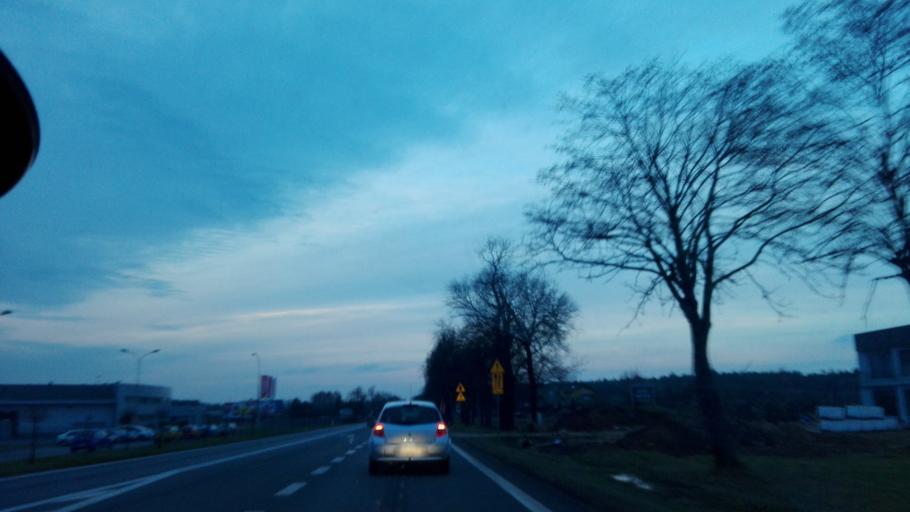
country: PL
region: Masovian Voivodeship
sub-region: Powiat siedlecki
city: Skorzec
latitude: 52.1797
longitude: 22.1675
